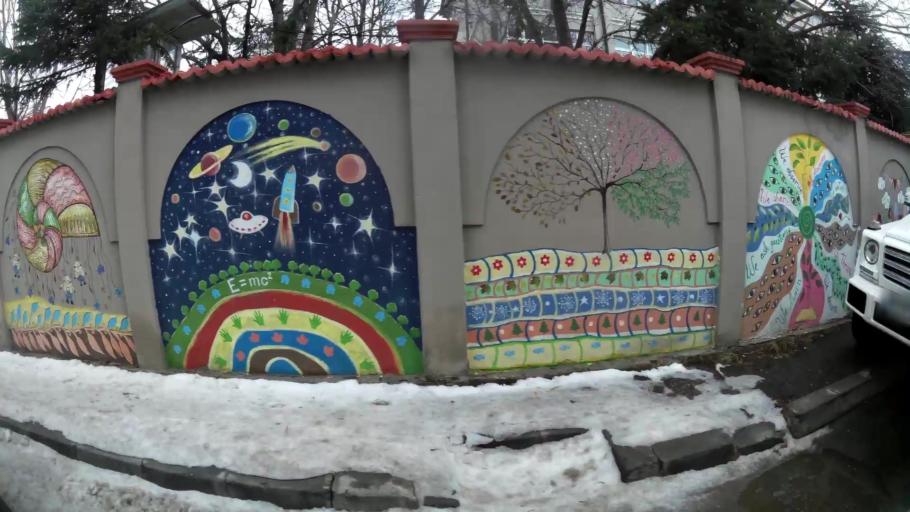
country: RO
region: Bucuresti
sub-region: Municipiul Bucuresti
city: Bucharest
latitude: 44.4090
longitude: 26.1275
